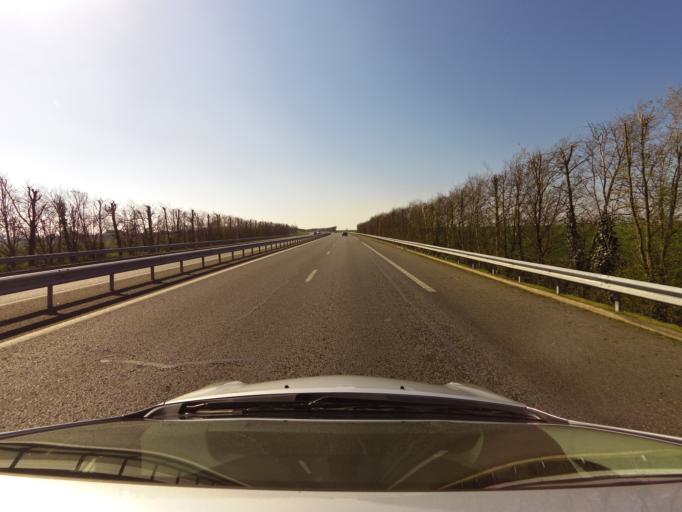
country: FR
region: Brittany
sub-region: Departement d'Ille-et-Vilaine
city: Plelan-le-Grand
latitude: 47.9779
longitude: -2.0981
